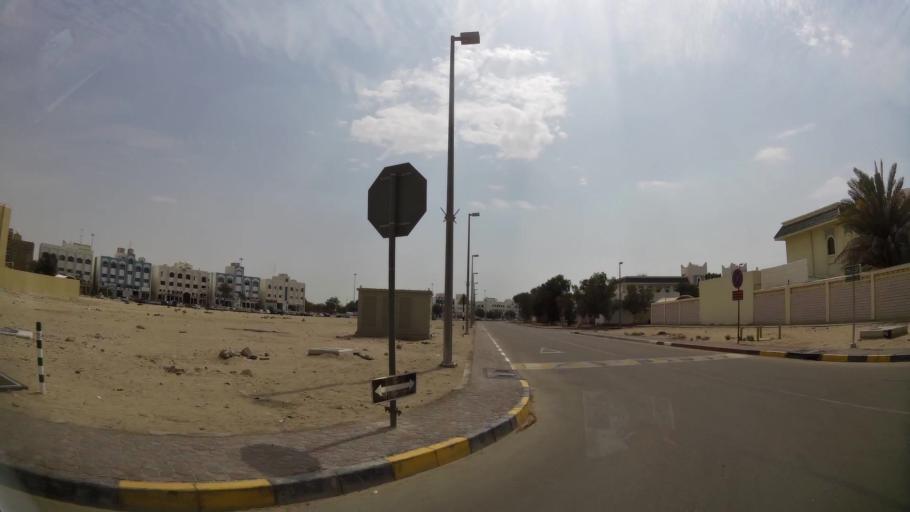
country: AE
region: Abu Dhabi
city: Abu Dhabi
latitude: 24.5349
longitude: 54.6896
